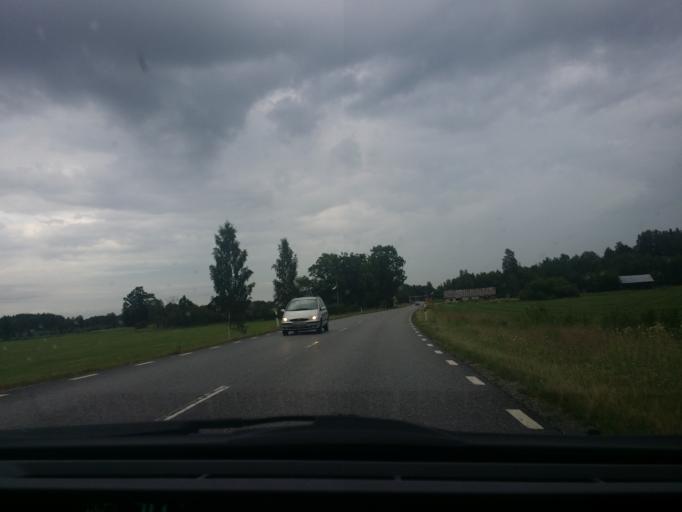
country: SE
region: OErebro
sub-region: Lindesbergs Kommun
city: Frovi
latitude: 59.4438
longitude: 15.2861
